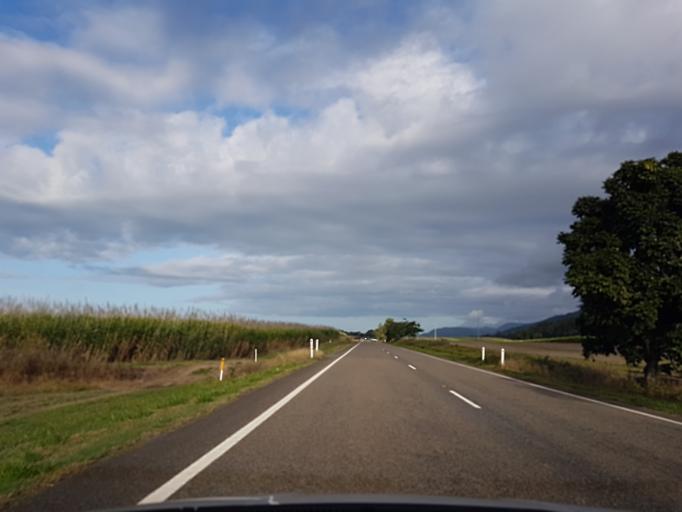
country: AU
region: Queensland
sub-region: Cairns
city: Port Douglas
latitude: -16.4838
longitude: 145.4118
